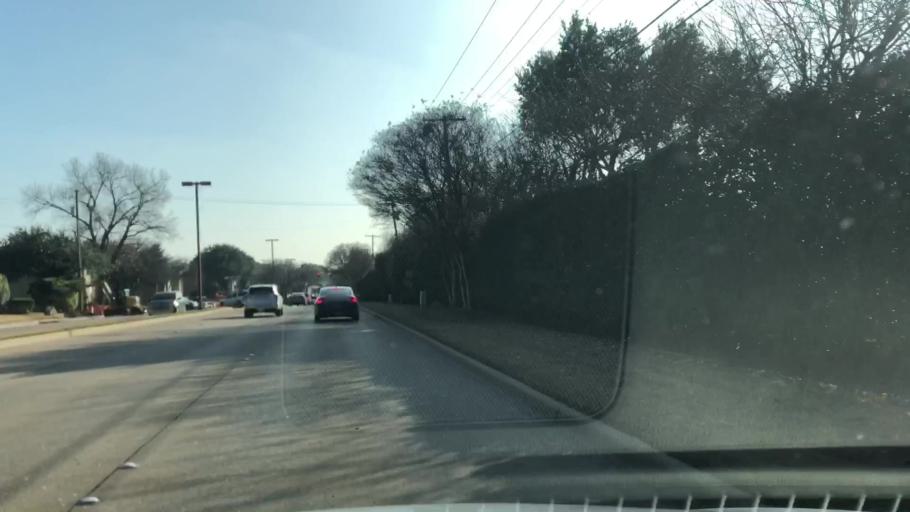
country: US
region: Texas
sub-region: Dallas County
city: Addison
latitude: 32.9433
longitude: -96.8558
